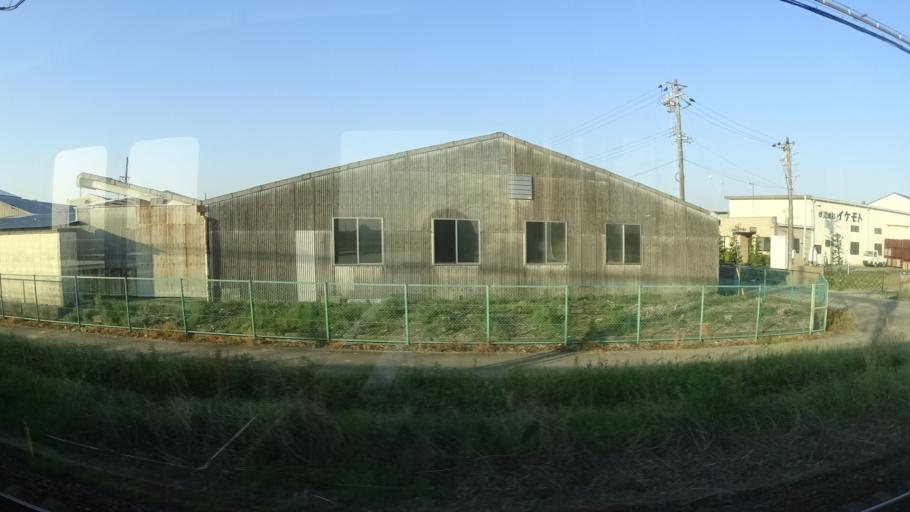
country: JP
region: Mie
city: Hisai-motomachi
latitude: 34.5569
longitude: 136.5645
